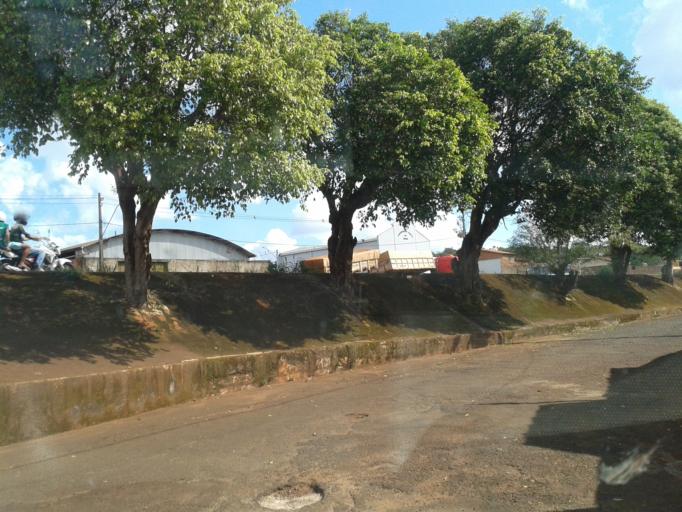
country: BR
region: Minas Gerais
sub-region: Capinopolis
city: Capinopolis
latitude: -18.6867
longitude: -49.5790
